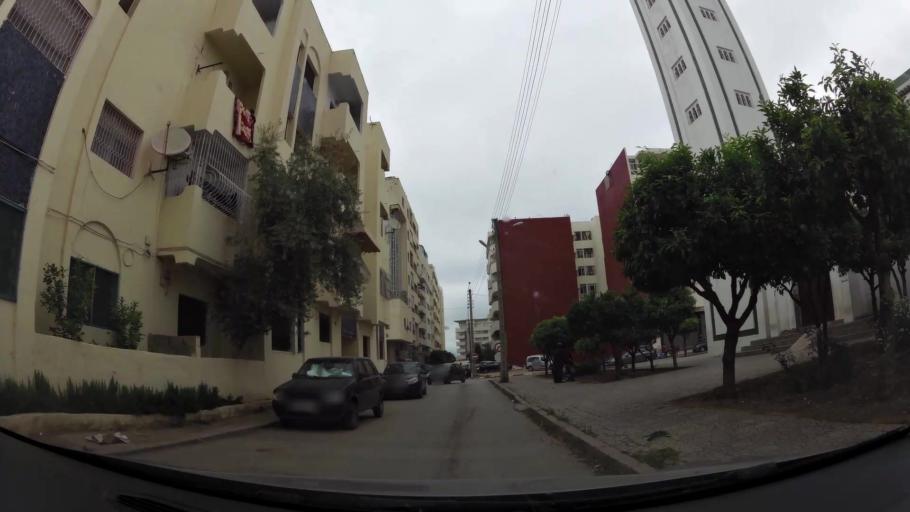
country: MA
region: Fes-Boulemane
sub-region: Fes
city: Fes
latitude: 34.0302
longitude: -5.0081
